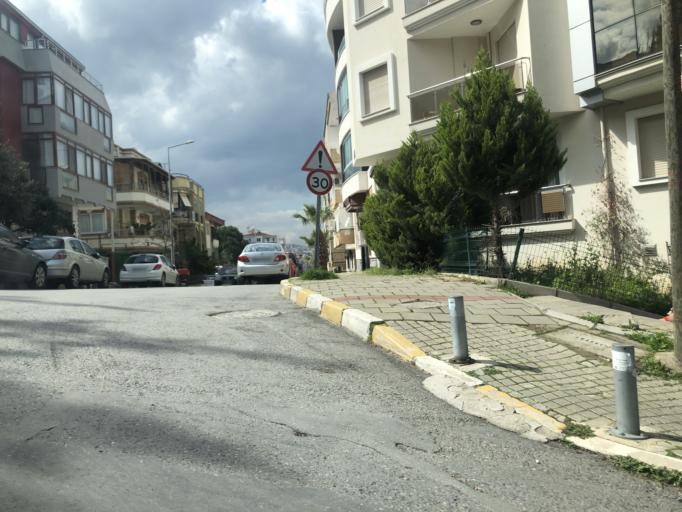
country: TR
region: Izmir
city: Karabaglar
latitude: 38.3923
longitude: 27.0447
